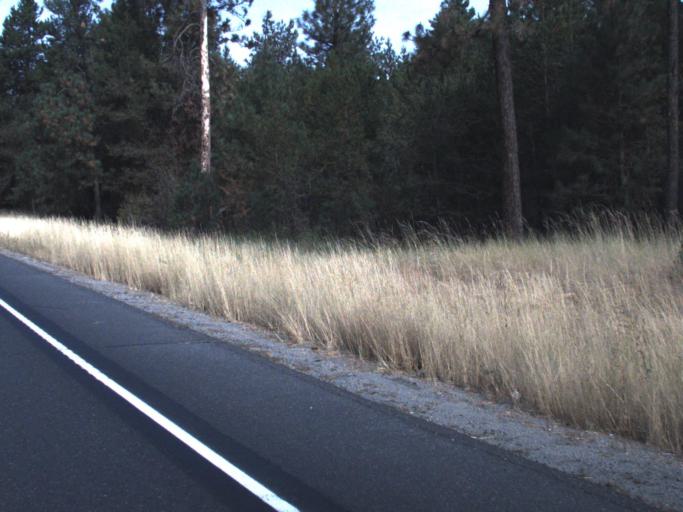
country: US
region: Washington
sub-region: Spokane County
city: Deer Park
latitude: 47.8918
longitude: -117.4284
